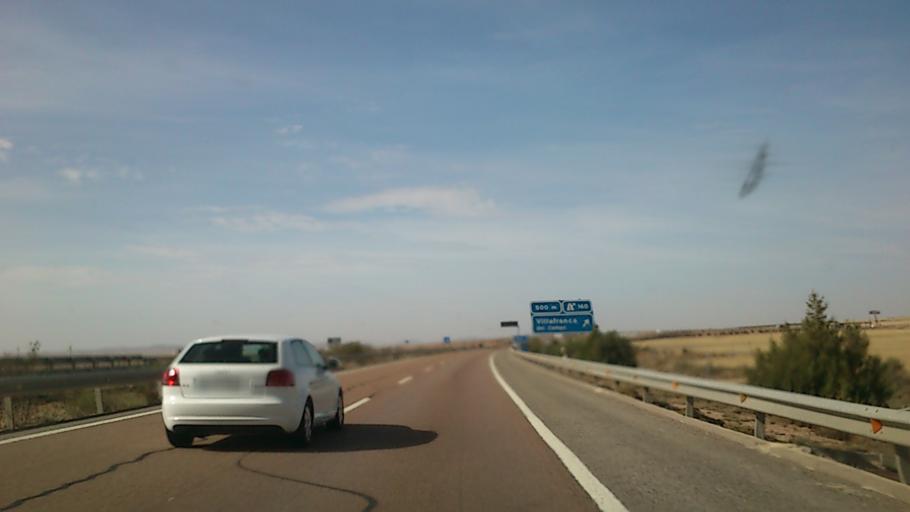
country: ES
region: Aragon
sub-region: Provincia de Teruel
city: Villafranca del Campo
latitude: 40.6911
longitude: -1.3198
